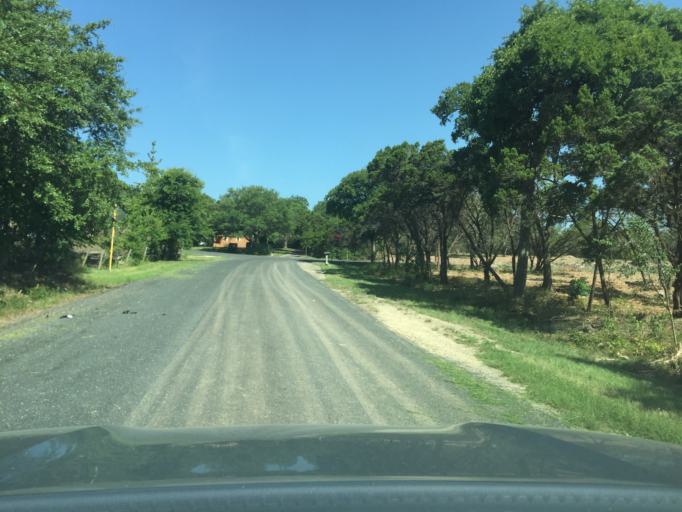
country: US
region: Texas
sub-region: Bexar County
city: Timberwood Park
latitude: 29.7130
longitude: -98.4694
